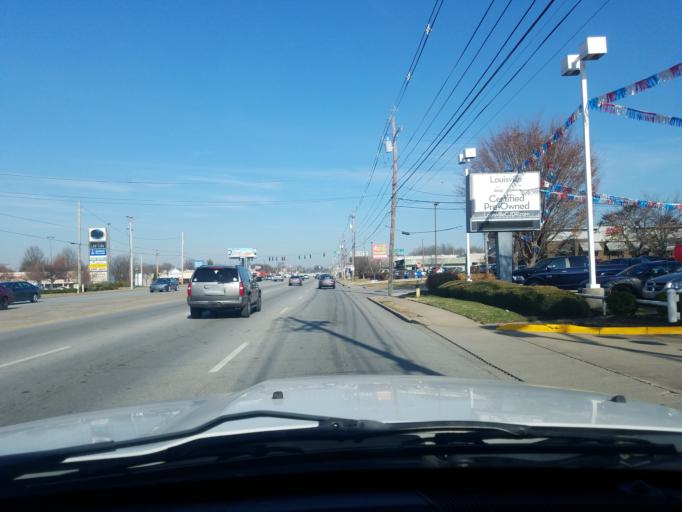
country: US
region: Kentucky
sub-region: Jefferson County
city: Pleasure Ridge Park
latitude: 38.1608
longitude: -85.8322
